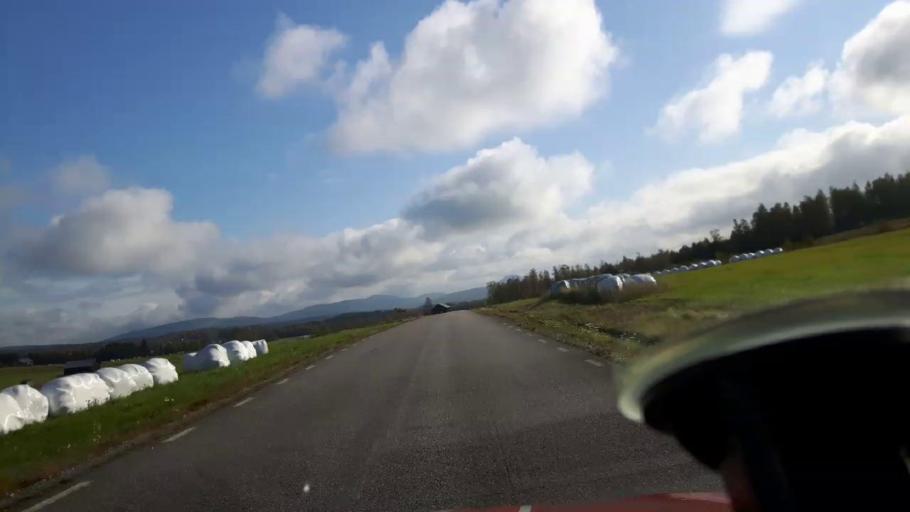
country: SE
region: Gaevleborg
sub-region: Ljusdals Kommun
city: Ljusdal
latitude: 61.7627
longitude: 16.0715
